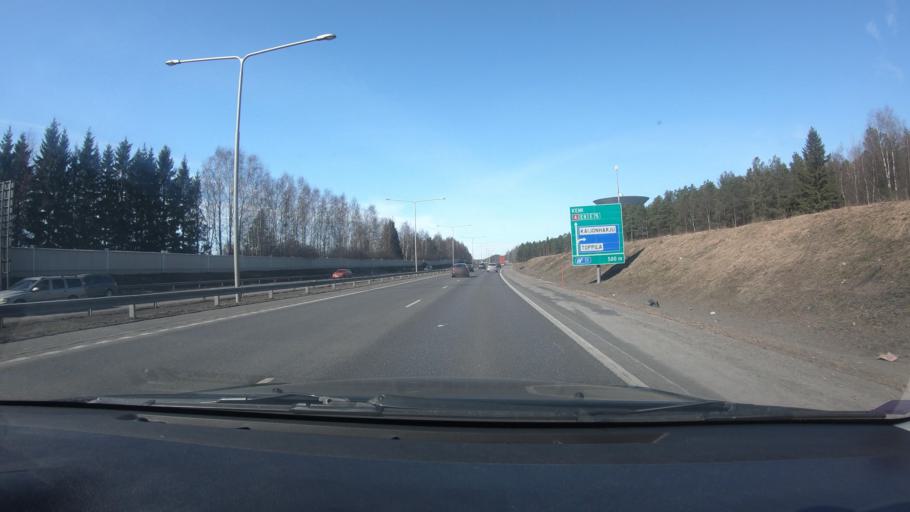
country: FI
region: Northern Ostrobothnia
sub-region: Oulu
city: Oulu
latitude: 65.0340
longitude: 25.4904
